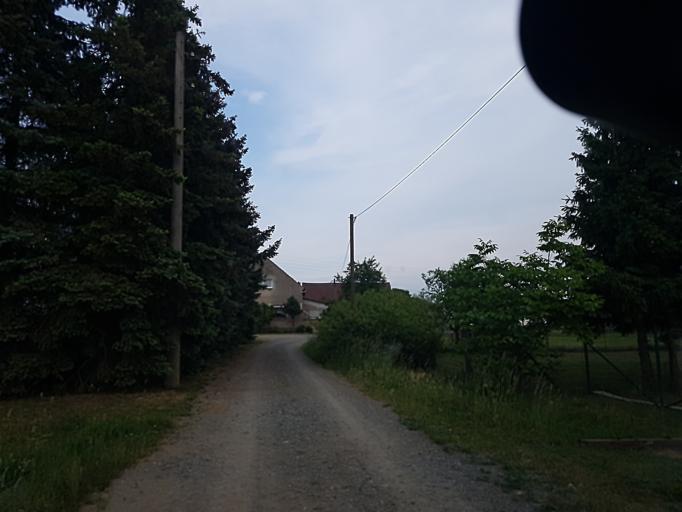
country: DE
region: Saxony-Anhalt
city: Holzdorf
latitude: 51.7407
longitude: 13.1715
